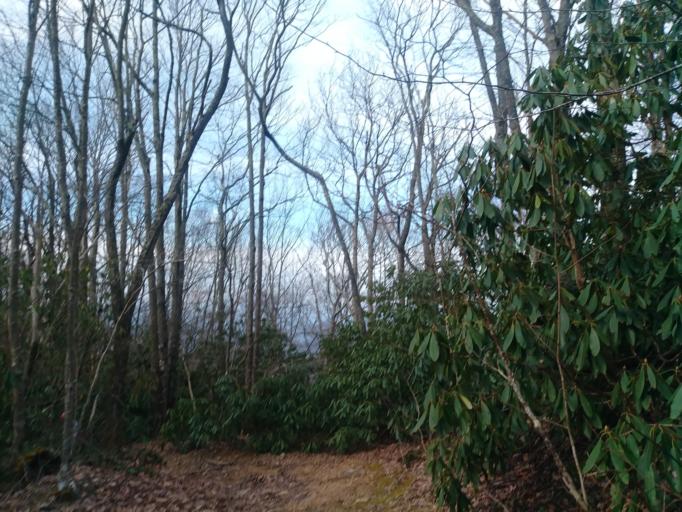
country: US
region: Tennessee
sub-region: Greene County
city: Tusculum
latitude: 36.0550
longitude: -82.6727
